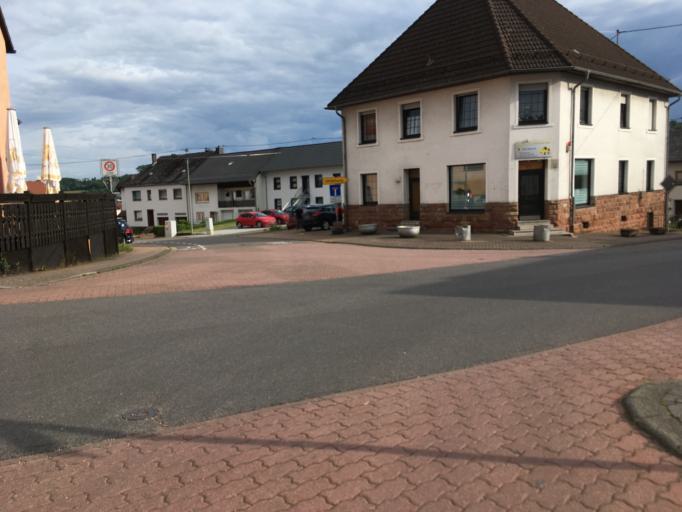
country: DE
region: Saarland
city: Losheim
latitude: 49.5117
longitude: 6.7465
